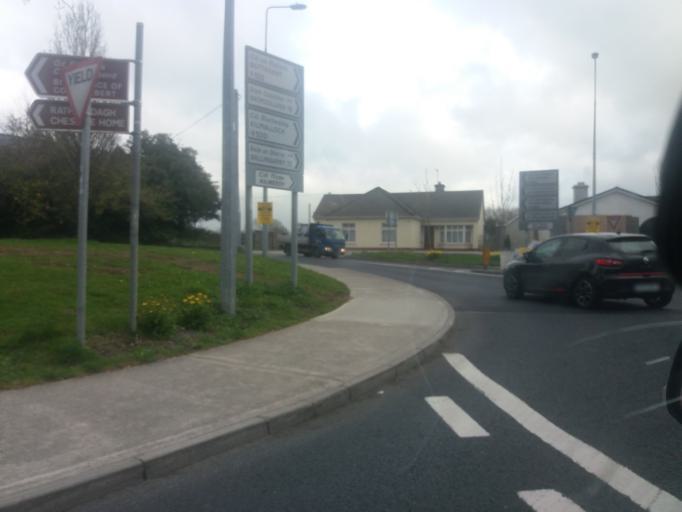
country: IE
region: Munster
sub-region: County Limerick
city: Newcastle West
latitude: 52.4494
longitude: -9.0496
